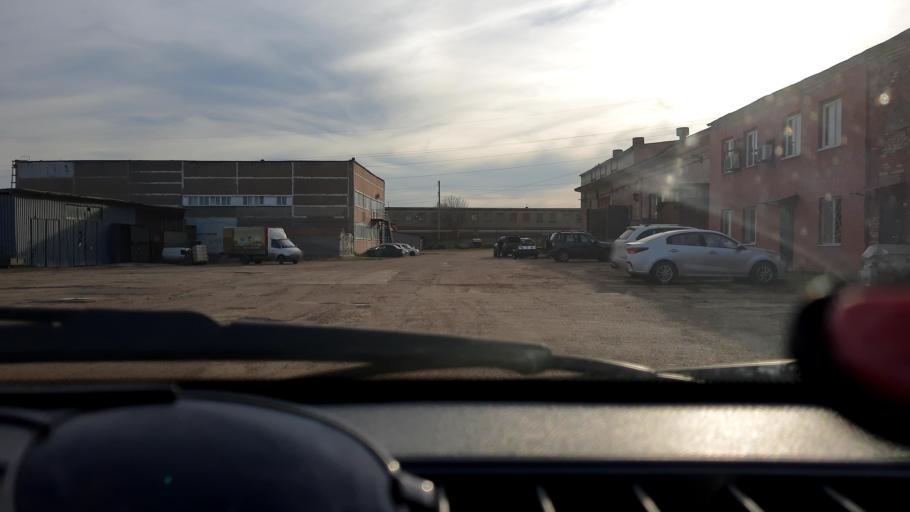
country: RU
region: Bashkortostan
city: Ufa
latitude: 54.8291
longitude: 56.1132
